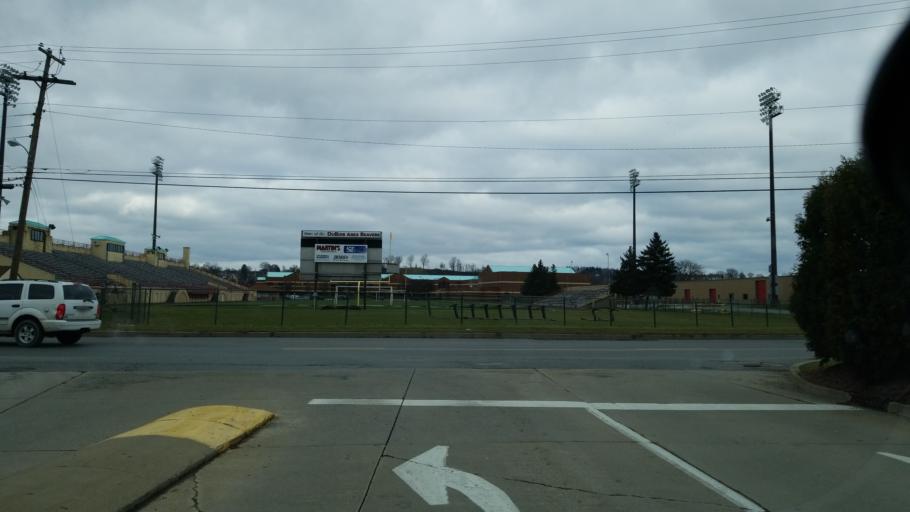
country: US
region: Pennsylvania
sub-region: Clearfield County
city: DuBois
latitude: 41.1207
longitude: -78.7569
